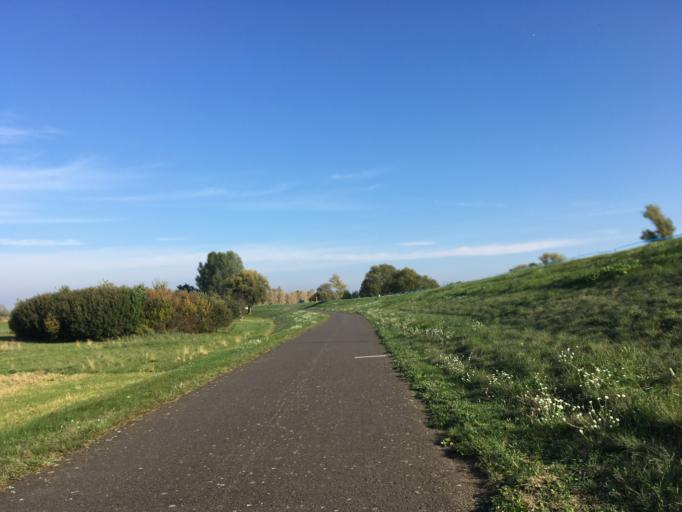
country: DE
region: Brandenburg
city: Reitwein
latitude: 52.5438
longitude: 14.6088
